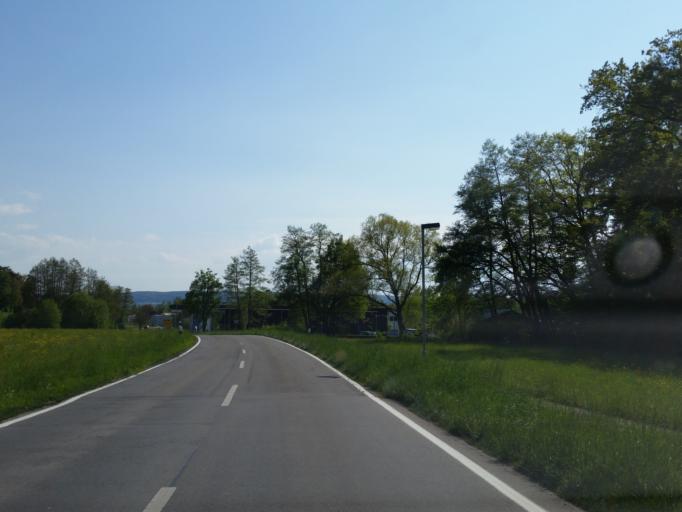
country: DE
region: Baden-Wuerttemberg
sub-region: Freiburg Region
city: Allensbach
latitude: 47.7268
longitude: 9.0748
